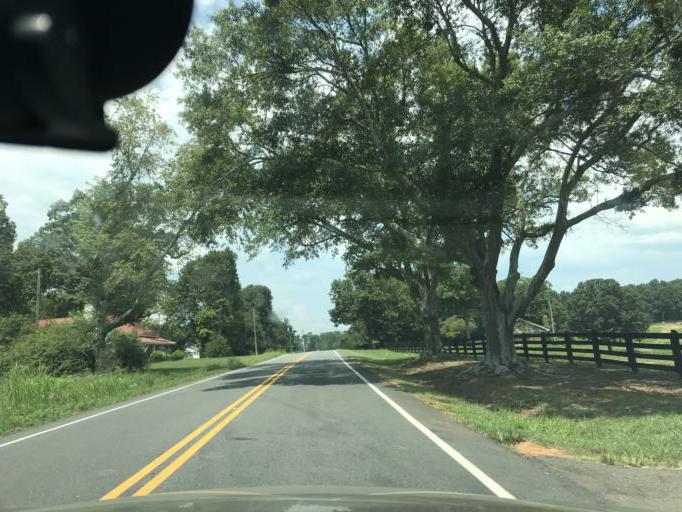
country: US
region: Georgia
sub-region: Dawson County
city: Dawsonville
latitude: 34.3360
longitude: -84.1338
